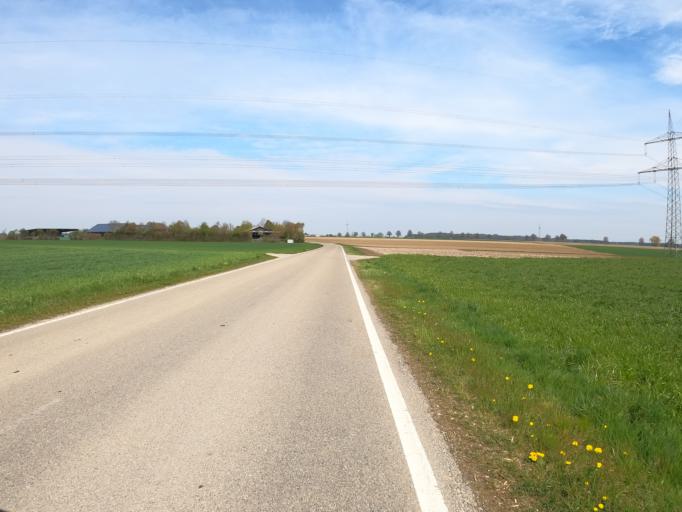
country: DE
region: Bavaria
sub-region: Swabia
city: Rieden an der Kotz
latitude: 48.3867
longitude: 10.2099
